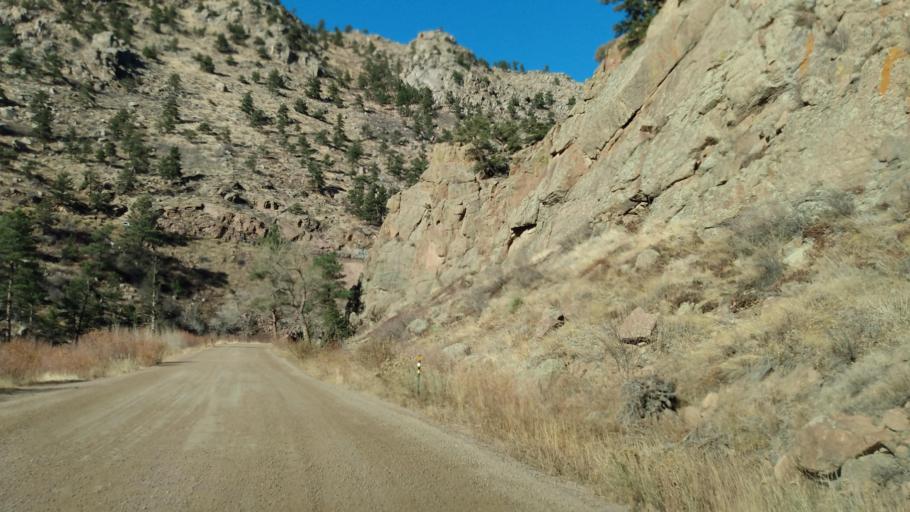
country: US
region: Colorado
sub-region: Boulder County
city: Lyons
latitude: 40.2372
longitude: -105.3191
